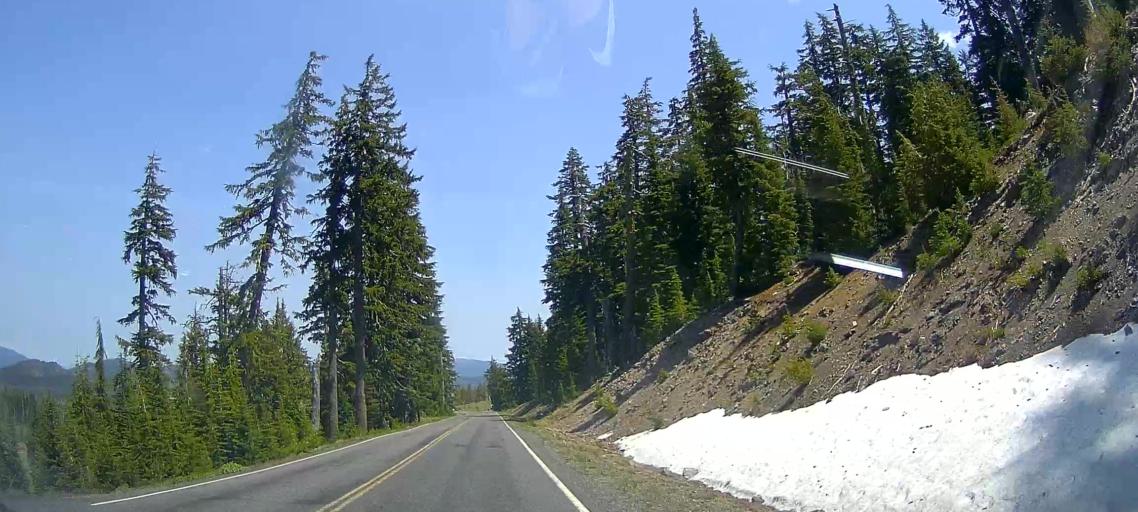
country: US
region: Oregon
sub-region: Jackson County
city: Shady Cove
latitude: 42.9870
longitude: -122.1453
